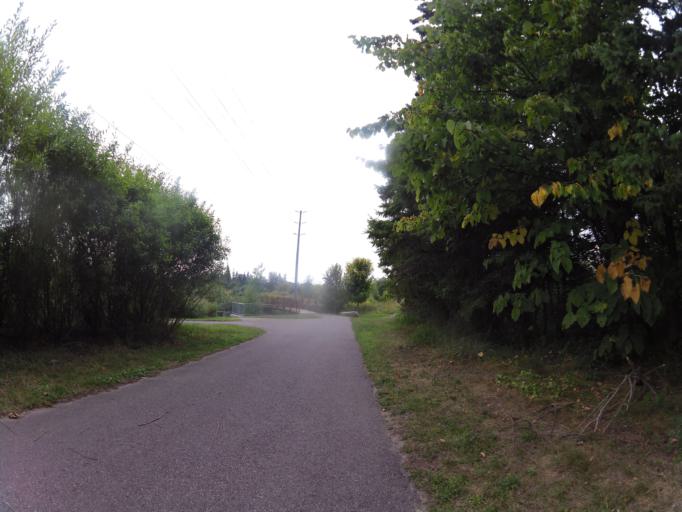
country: CA
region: Ontario
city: Bells Corners
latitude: 45.2793
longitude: -75.9355
